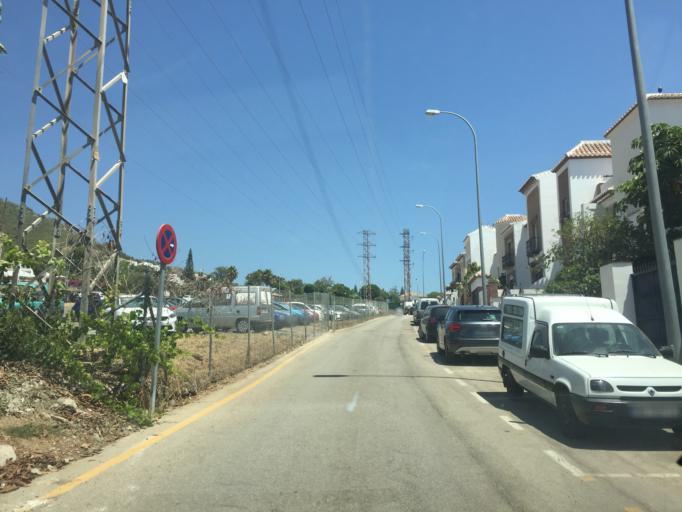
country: ES
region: Andalusia
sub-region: Provincia de Malaga
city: Nerja
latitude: 36.7643
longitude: -3.8731
